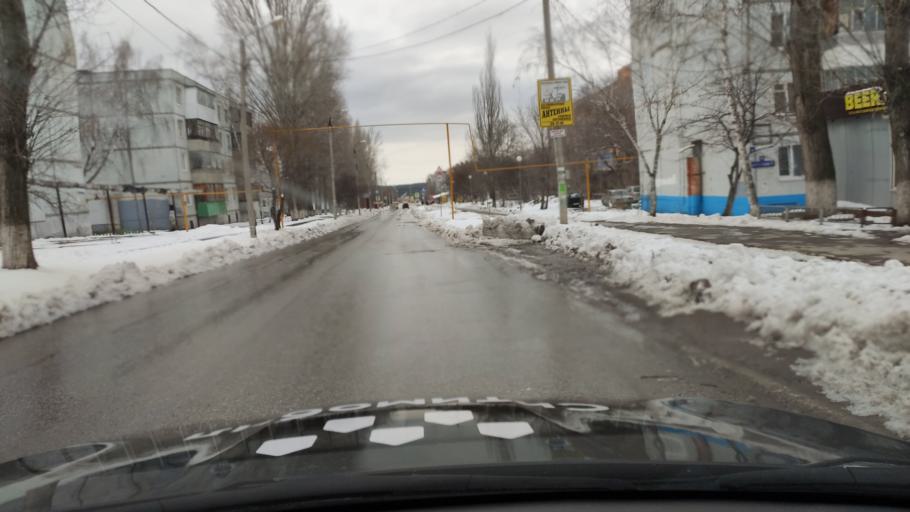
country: RU
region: Samara
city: Povolzhskiy
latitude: 53.5873
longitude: 49.7647
